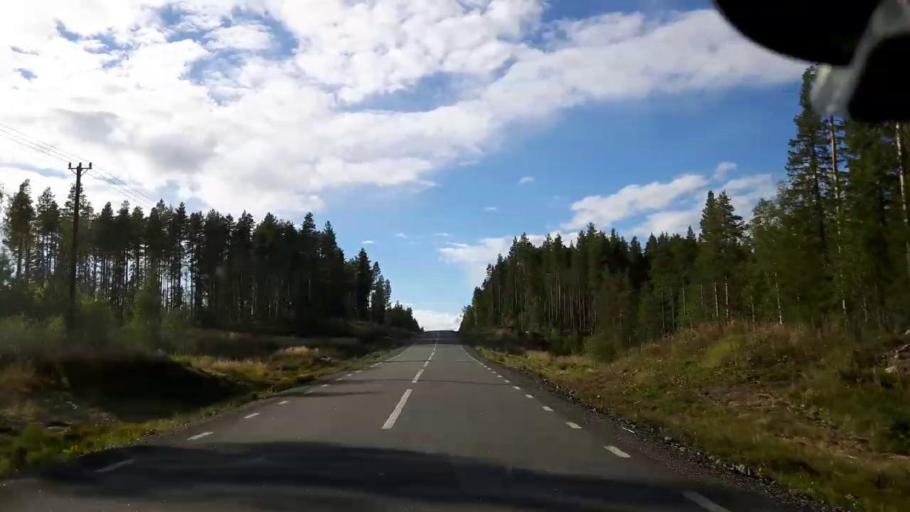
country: SE
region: Jaemtland
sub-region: Stroemsunds Kommun
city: Stroemsund
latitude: 63.5625
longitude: 15.8002
